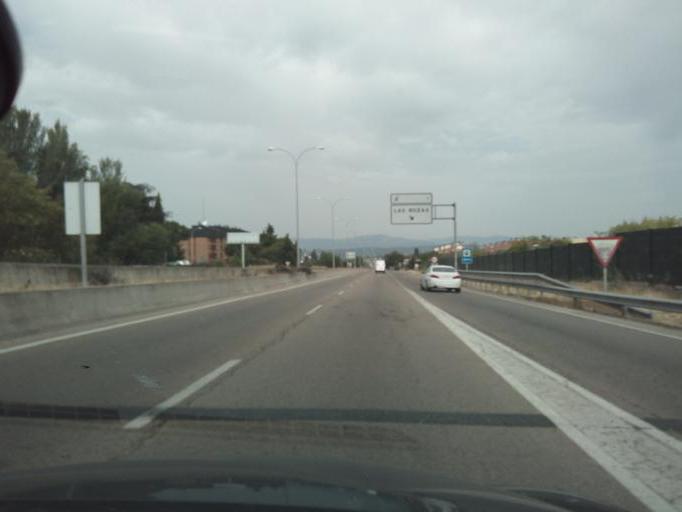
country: ES
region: Madrid
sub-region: Provincia de Madrid
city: Las Rozas de Madrid
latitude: 40.4883
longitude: -3.8710
